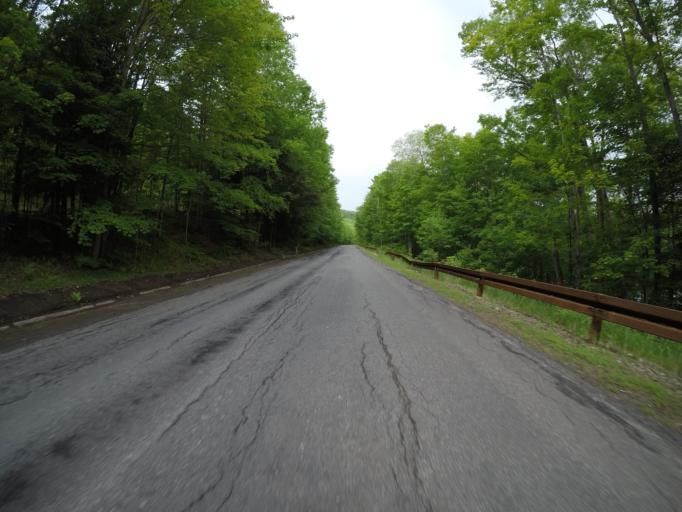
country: US
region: New York
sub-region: Sullivan County
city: Livingston Manor
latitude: 42.0844
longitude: -74.8122
